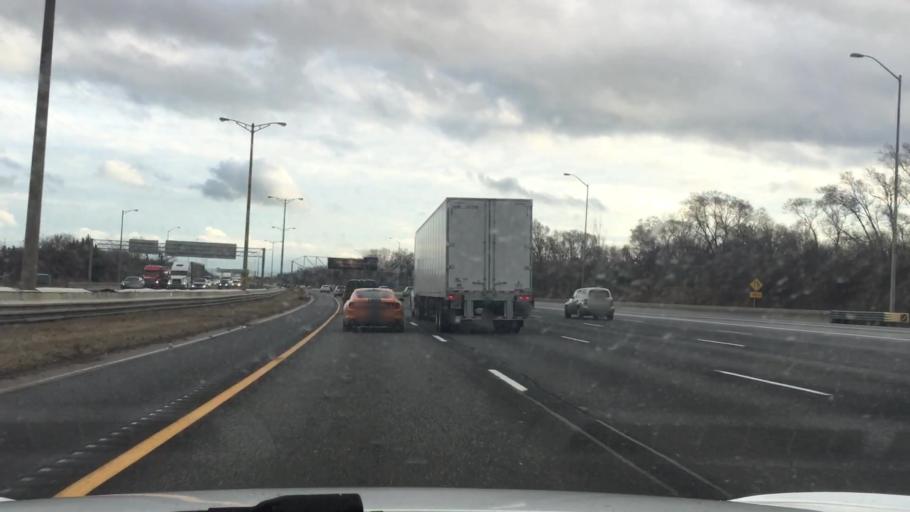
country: CA
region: Ontario
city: Burlington
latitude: 43.3251
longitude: -79.8235
